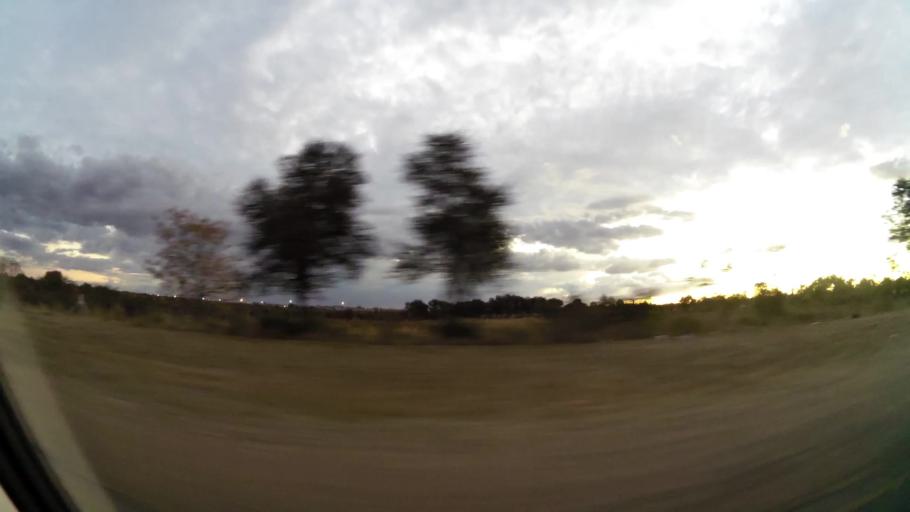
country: ZA
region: Limpopo
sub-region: Capricorn District Municipality
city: Polokwane
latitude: -23.8241
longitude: 29.4257
